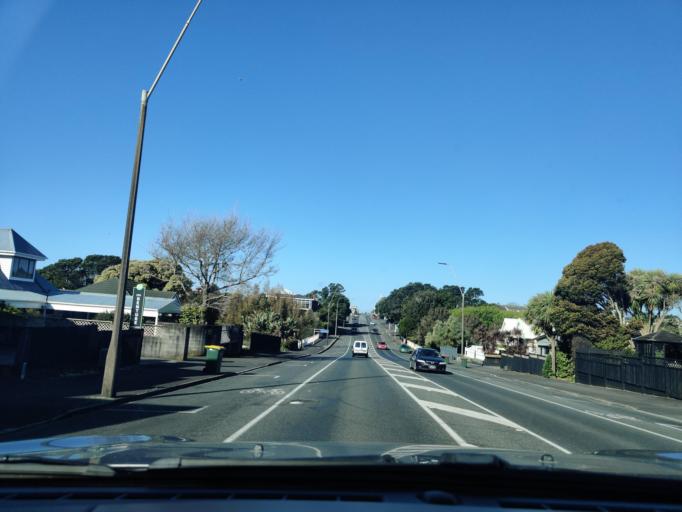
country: NZ
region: Taranaki
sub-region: New Plymouth District
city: New Plymouth
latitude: -39.0527
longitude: 174.0907
